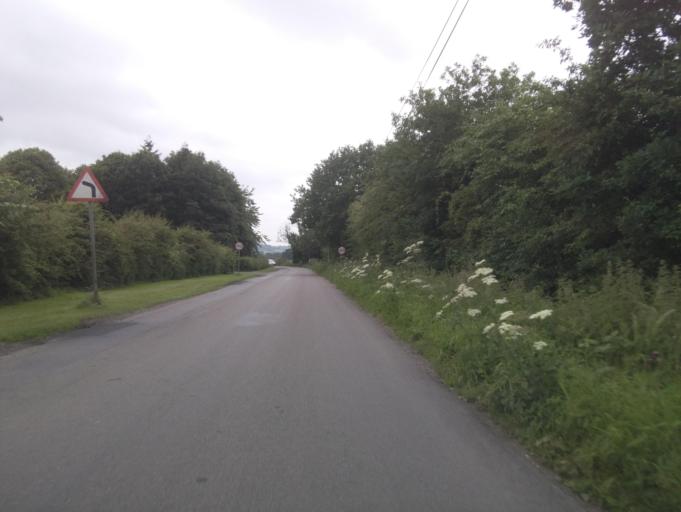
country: GB
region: England
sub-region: Derbyshire
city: Rodsley
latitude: 52.8794
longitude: -1.7129
